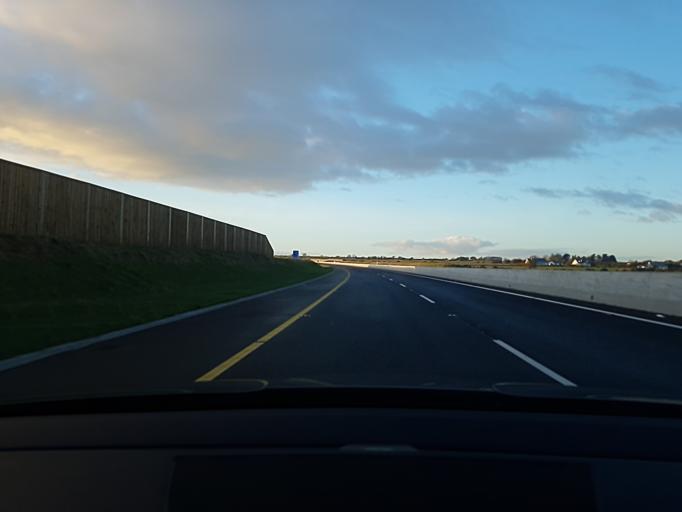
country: IE
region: Connaught
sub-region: County Galway
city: Athenry
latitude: 53.3937
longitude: -8.8042
